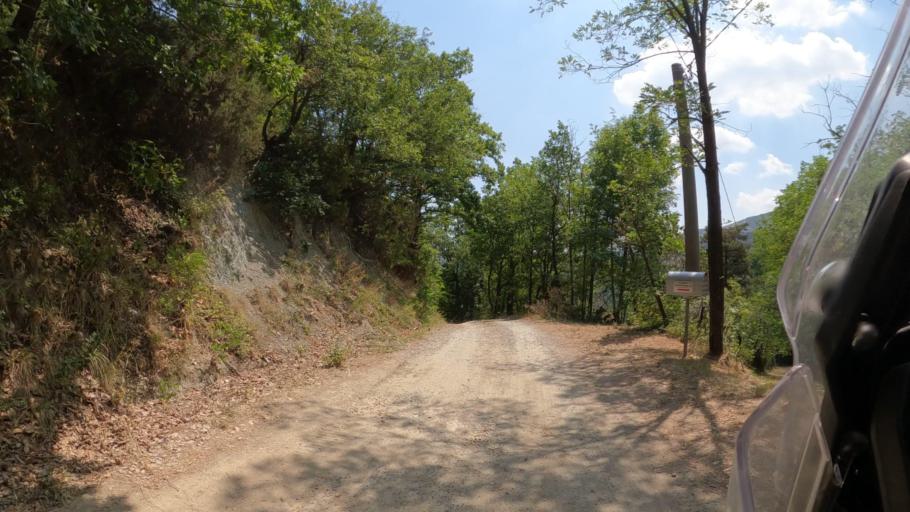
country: IT
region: Piedmont
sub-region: Provincia di Alessandria
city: Cassinelle-Concentrico
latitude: 44.5697
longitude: 8.5594
